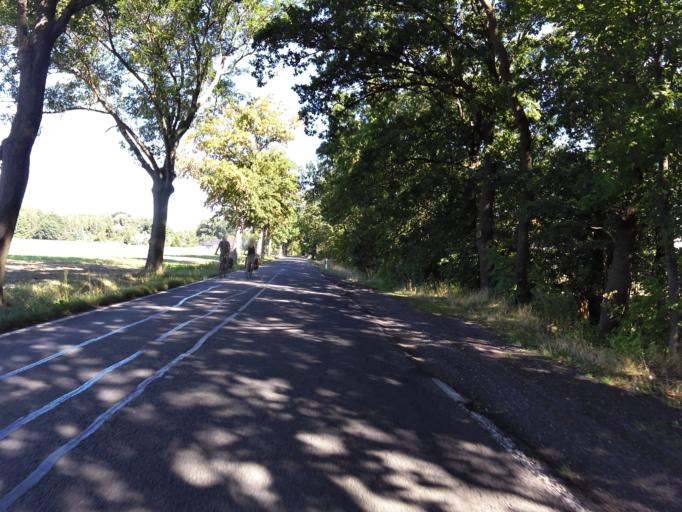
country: DE
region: Saxony-Anhalt
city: Pretzsch
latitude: 51.6822
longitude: 12.8269
